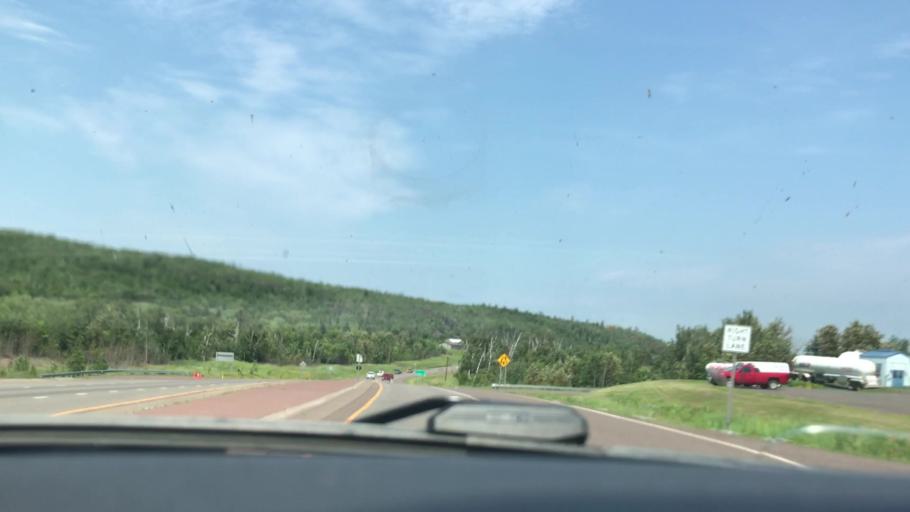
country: US
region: Minnesota
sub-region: Lake County
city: Silver Bay
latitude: 47.2953
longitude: -91.2566
